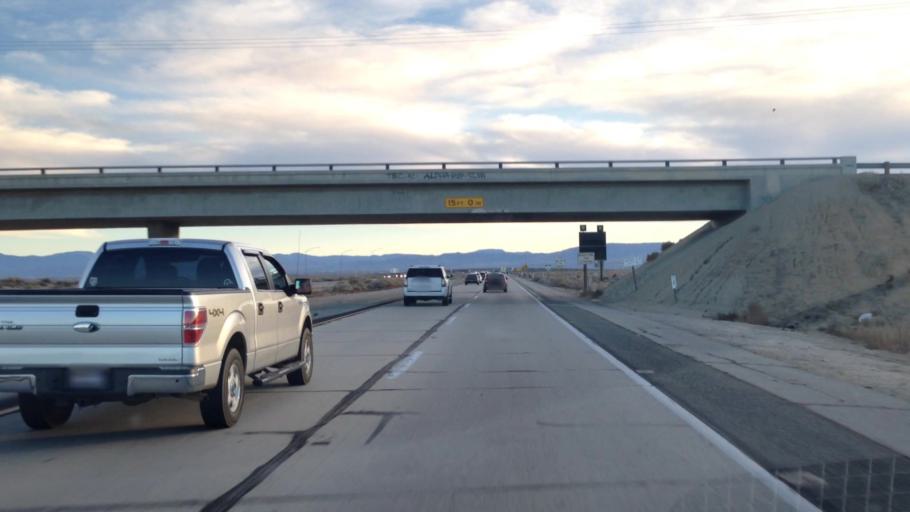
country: US
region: California
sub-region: Kern County
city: Rosamond
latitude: 34.8210
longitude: -118.1706
